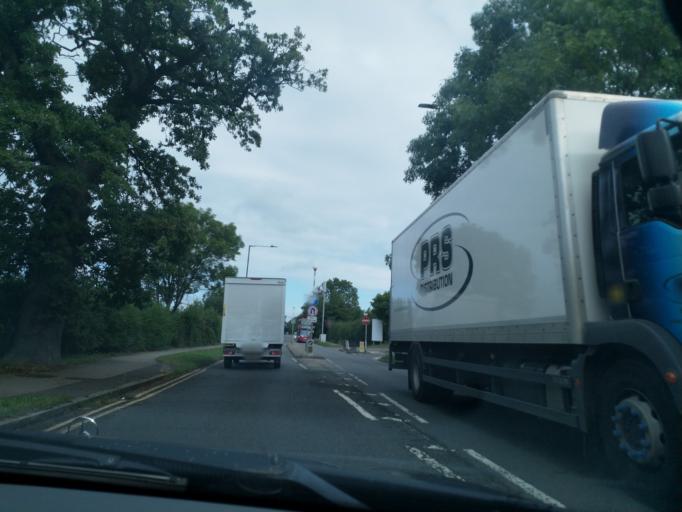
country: GB
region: England
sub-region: Greater London
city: Harrow on the Hill
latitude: 51.5707
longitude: -0.3229
